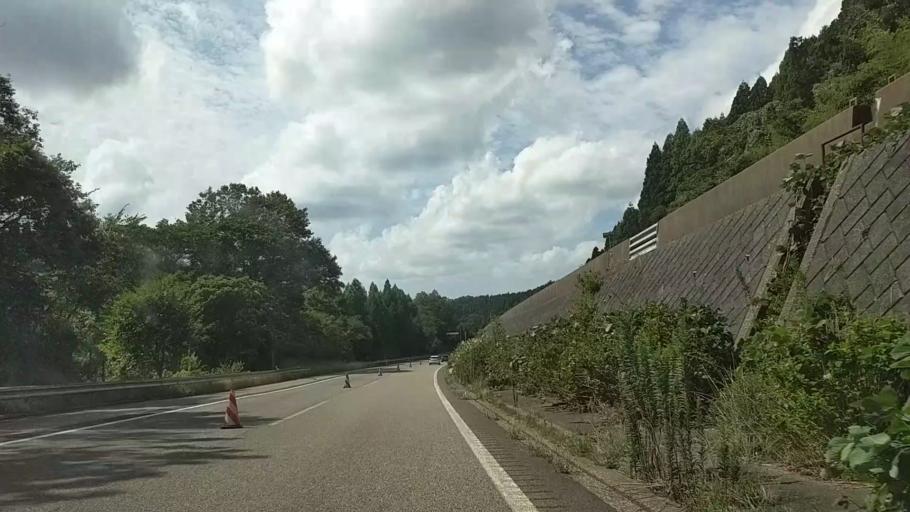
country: JP
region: Ishikawa
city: Tsubata
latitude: 36.5968
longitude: 136.7680
